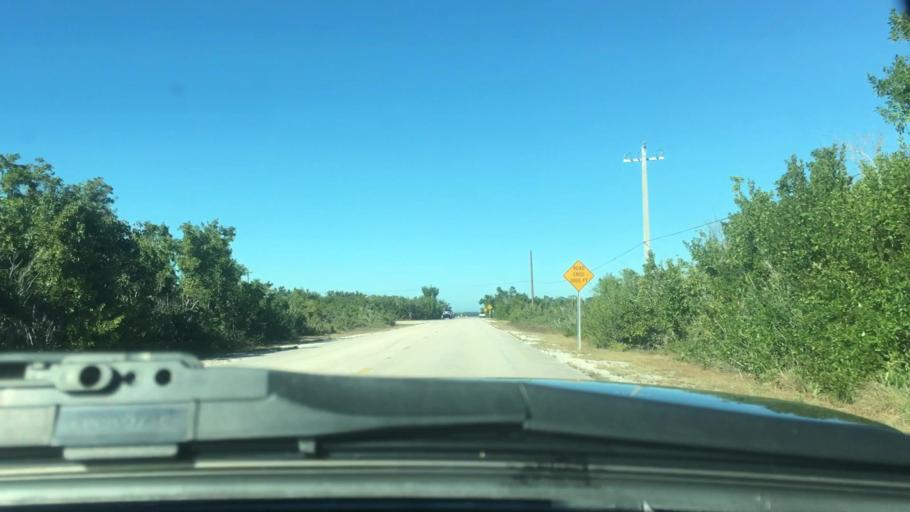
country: US
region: Florida
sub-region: Monroe County
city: Cudjoe Key
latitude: 24.6920
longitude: -81.4996
